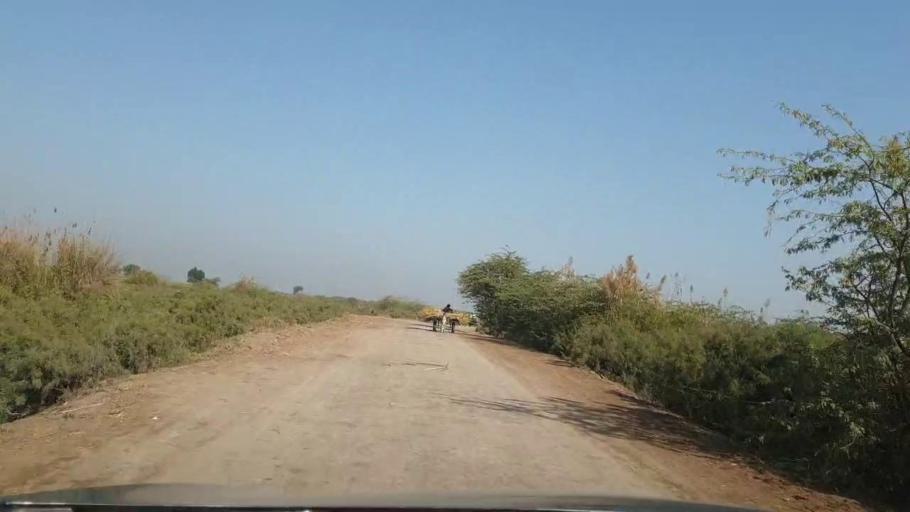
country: PK
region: Sindh
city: Mirpur Khas
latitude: 25.6505
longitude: 68.9090
